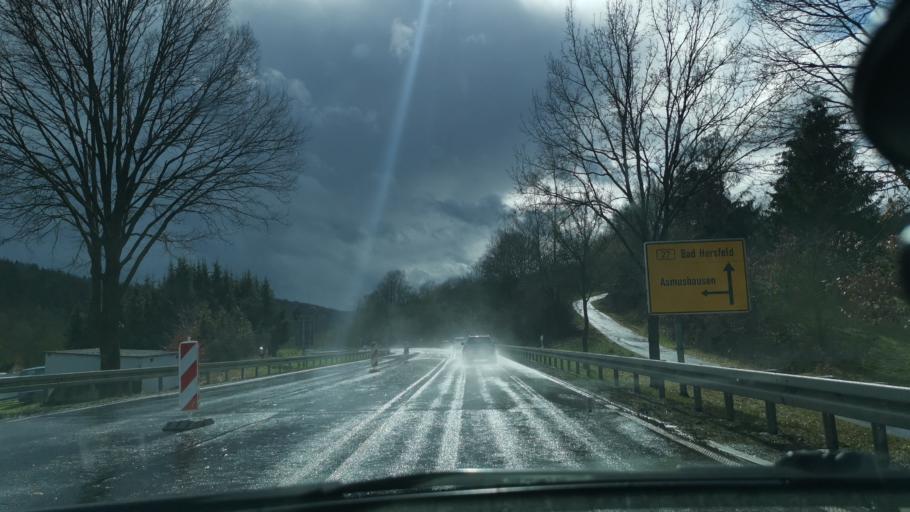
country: DE
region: Hesse
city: Bebra
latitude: 51.0065
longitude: 9.8141
